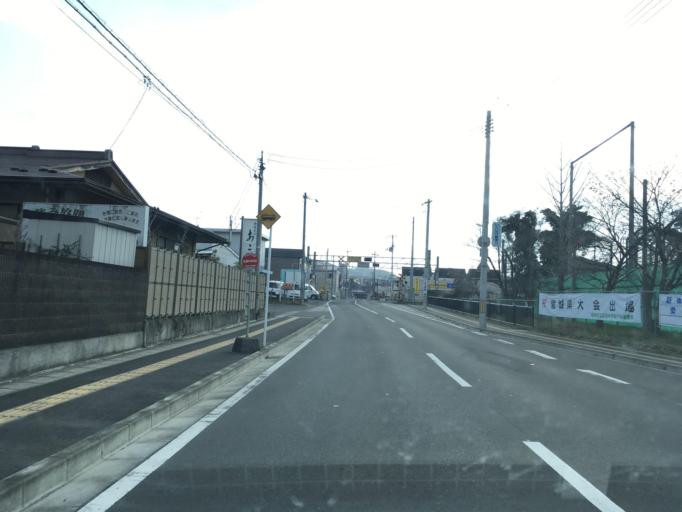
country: JP
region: Miyagi
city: Sendai
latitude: 38.2735
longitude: 140.7644
